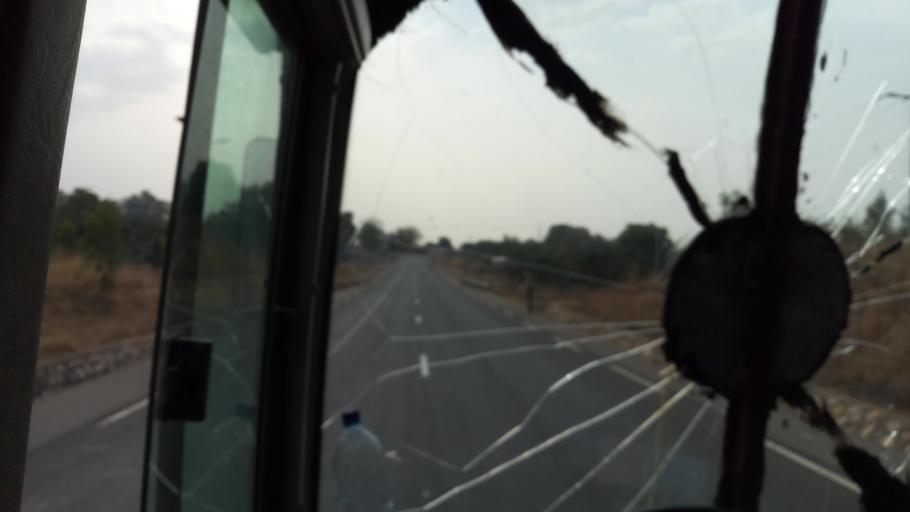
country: TG
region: Kara
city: Bafilo
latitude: 9.3624
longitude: 1.2432
